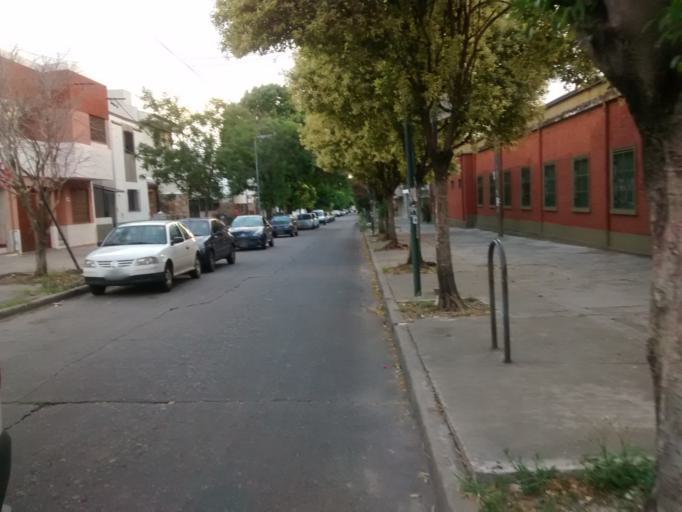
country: AR
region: Buenos Aires
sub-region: Partido de La Plata
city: La Plata
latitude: -34.9348
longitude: -57.9507
